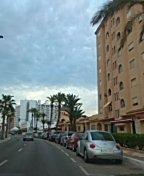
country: ES
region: Murcia
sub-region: Murcia
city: La Manga del Mar Menor
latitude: 37.6990
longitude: -0.7405
